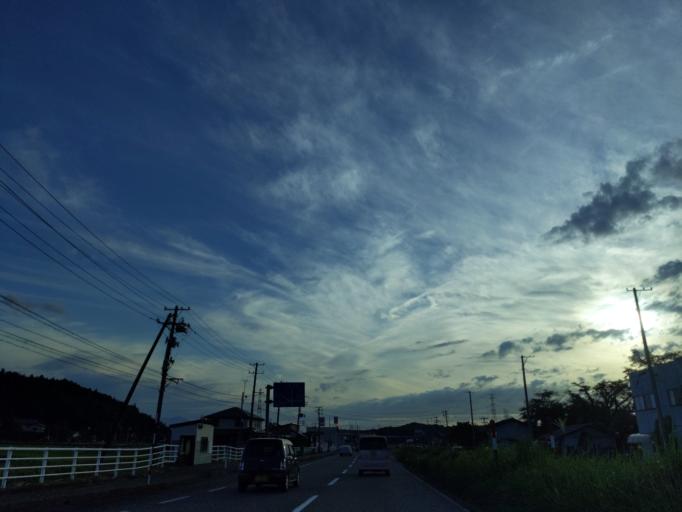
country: JP
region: Niigata
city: Kashiwazaki
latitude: 37.4485
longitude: 138.6433
